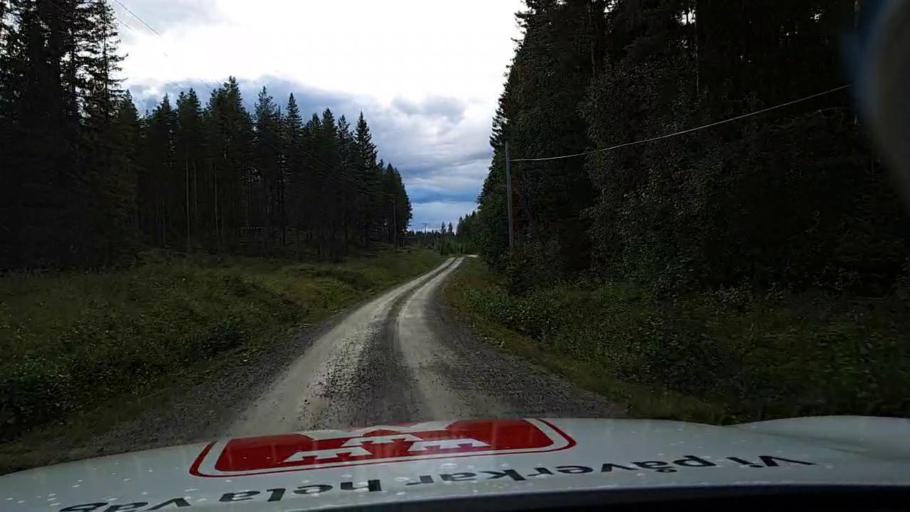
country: SE
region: Jaemtland
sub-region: Bergs Kommun
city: Hoverberg
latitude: 62.8805
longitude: 14.5967
